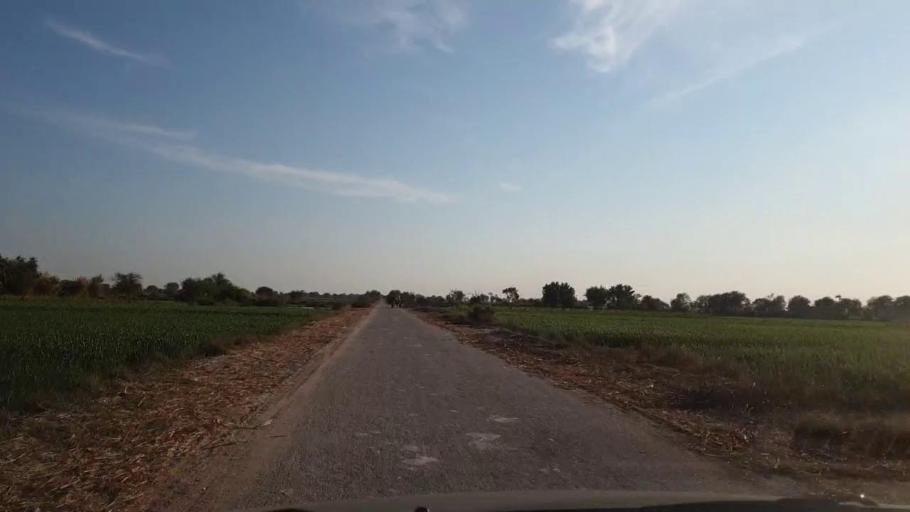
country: PK
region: Sindh
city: Khadro
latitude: 26.2009
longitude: 68.7467
